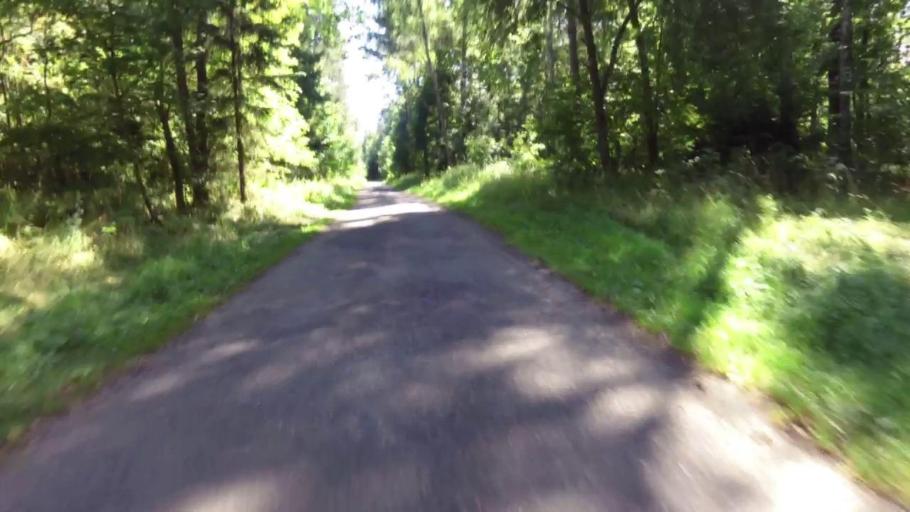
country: PL
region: West Pomeranian Voivodeship
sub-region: Powiat drawski
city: Czaplinek
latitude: 53.5192
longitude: 16.1835
